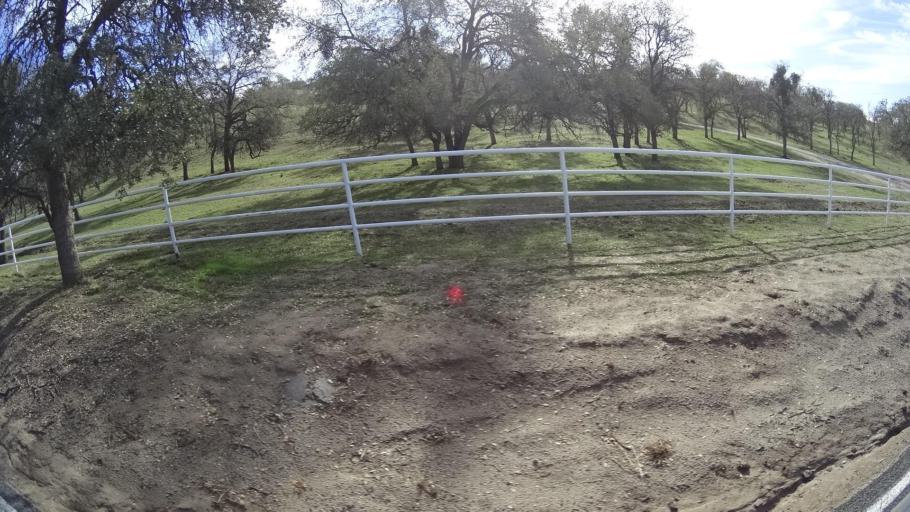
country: US
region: California
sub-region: Kern County
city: Oildale
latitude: 35.6285
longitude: -118.8221
